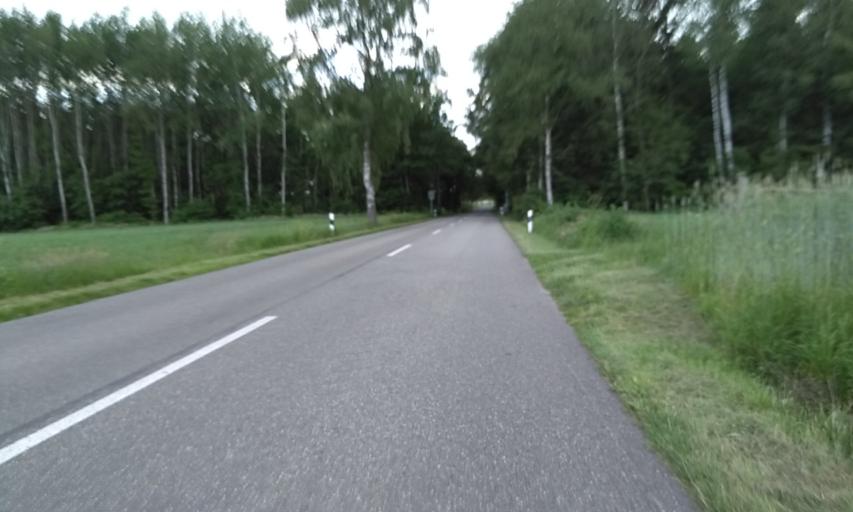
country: DE
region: Lower Saxony
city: Halvesbostel
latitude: 53.3569
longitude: 9.5719
